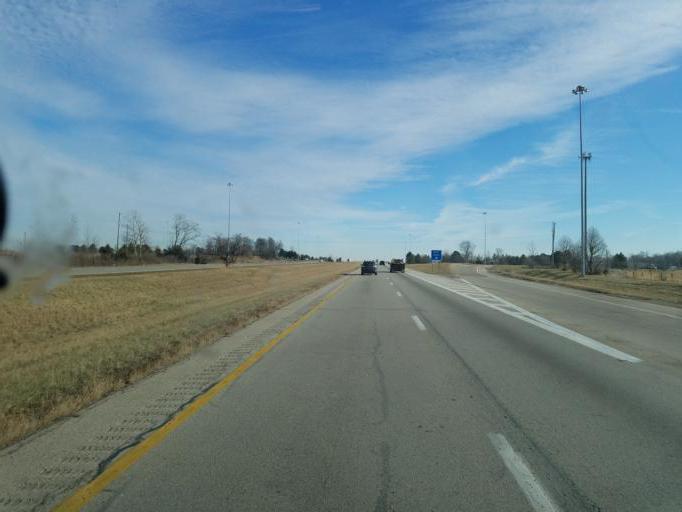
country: US
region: Ohio
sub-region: Preble County
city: New Paris
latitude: 39.8285
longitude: -84.7669
